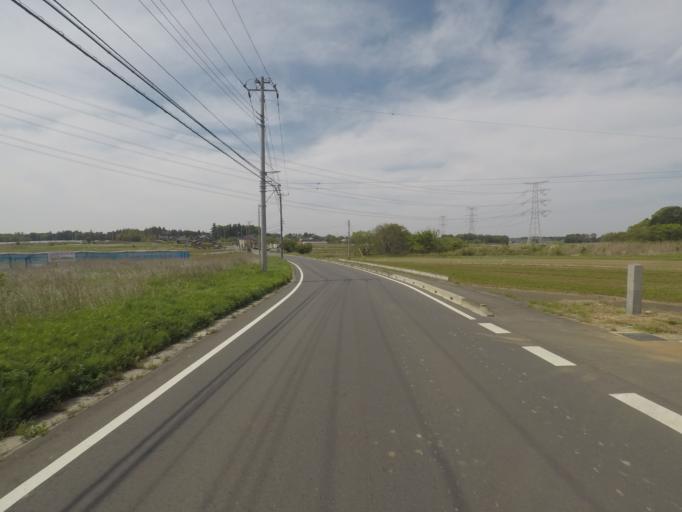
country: JP
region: Ibaraki
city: Ishige
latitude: 36.0819
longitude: 140.0365
